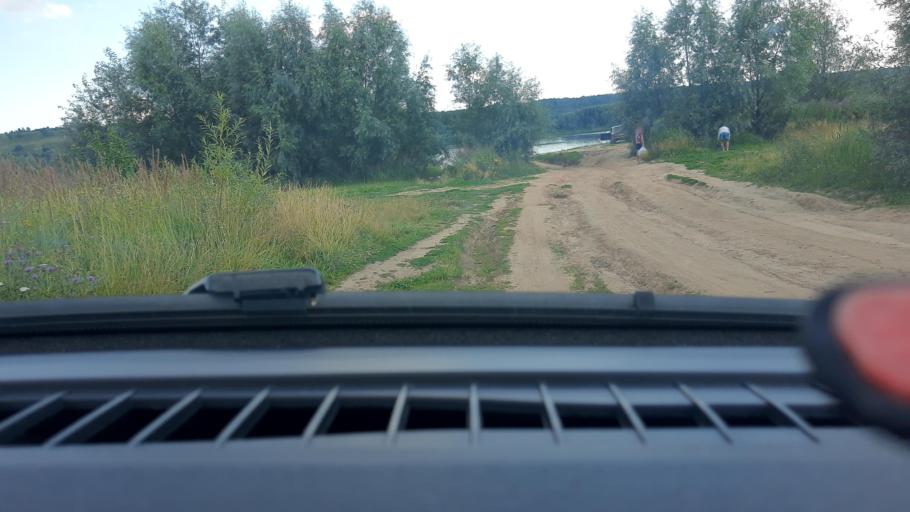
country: RU
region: Nizjnij Novgorod
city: Burevestnik
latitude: 56.1925
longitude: 43.7718
